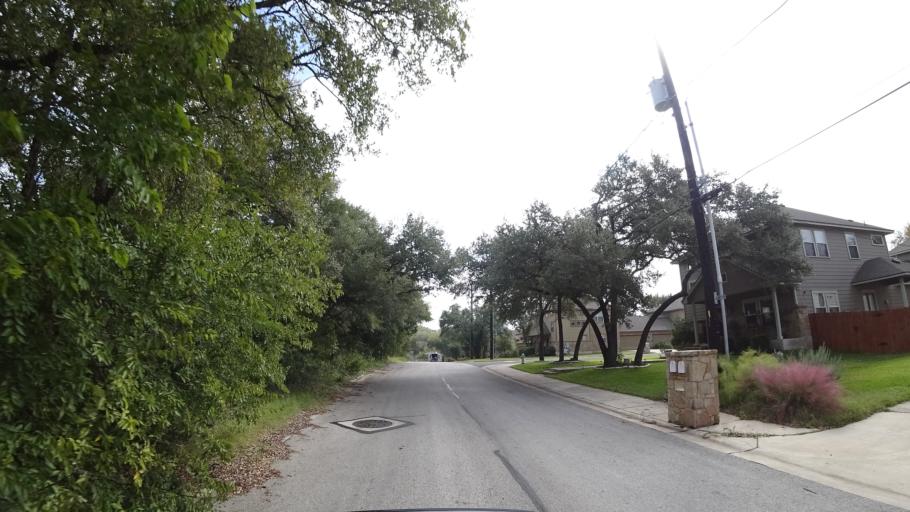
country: US
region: Texas
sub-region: Travis County
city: Shady Hollow
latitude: 30.2044
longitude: -97.8326
